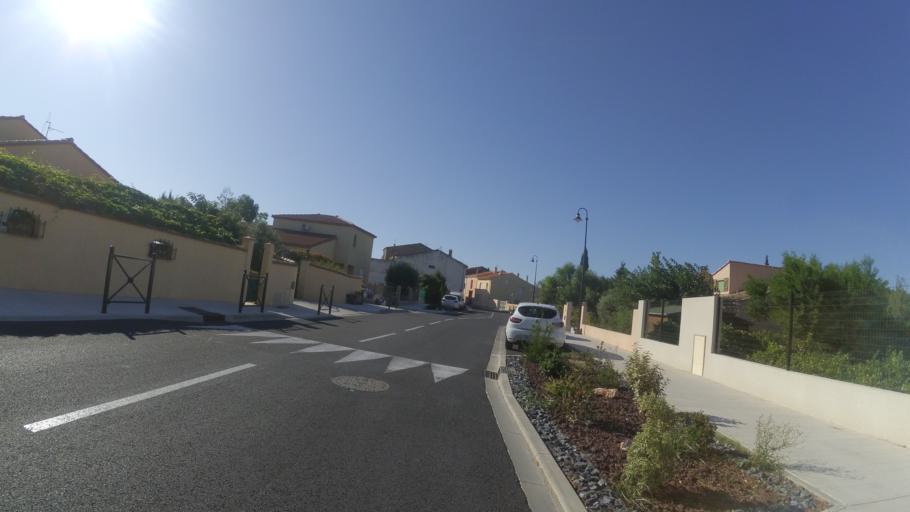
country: FR
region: Languedoc-Roussillon
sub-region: Departement des Pyrenees-Orientales
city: Villeneuve-la-Riviere
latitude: 42.6952
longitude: 2.8003
